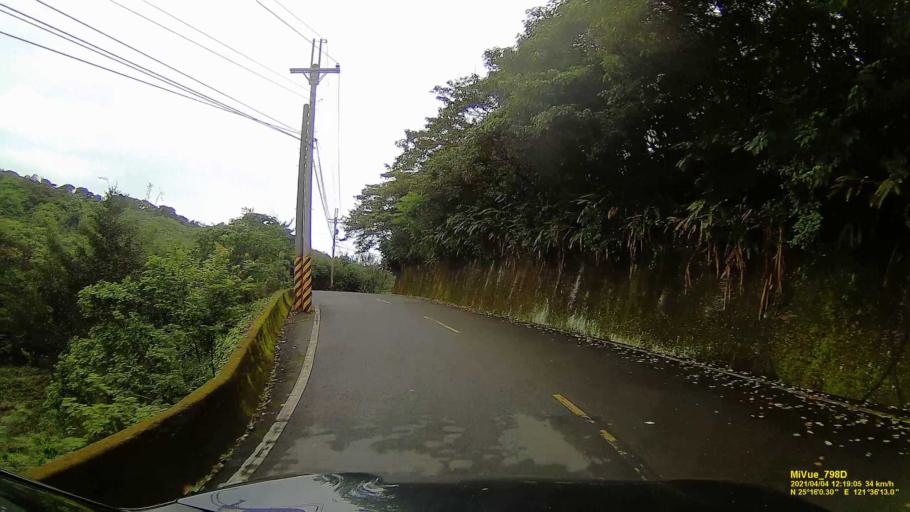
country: TW
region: Taiwan
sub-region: Keelung
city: Keelung
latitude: 25.2669
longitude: 121.6036
